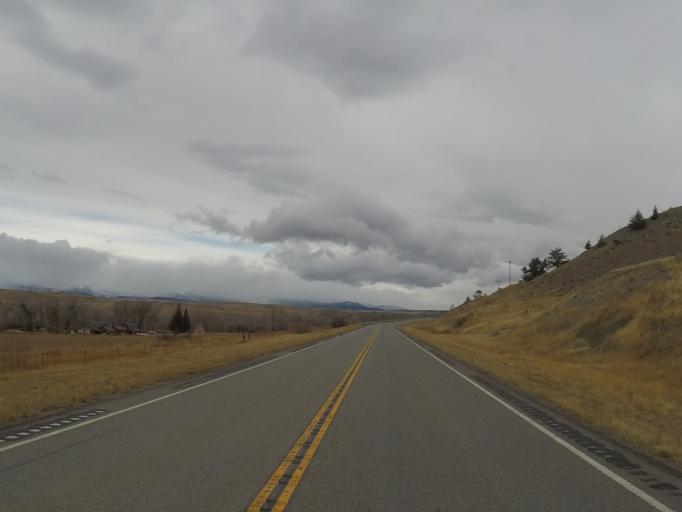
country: US
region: Montana
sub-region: Sweet Grass County
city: Big Timber
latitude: 45.8792
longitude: -109.9540
